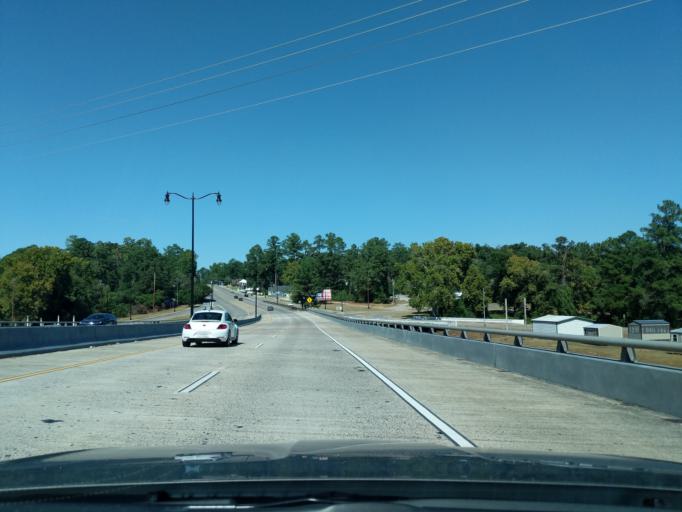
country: US
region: Georgia
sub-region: Richmond County
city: Augusta
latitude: 33.4908
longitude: -82.0099
